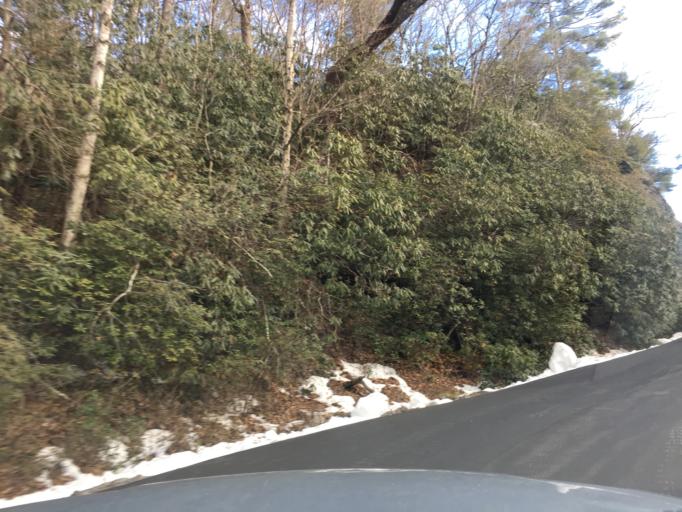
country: US
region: North Carolina
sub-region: Jackson County
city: Cullowhee
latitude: 35.1288
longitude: -83.0102
